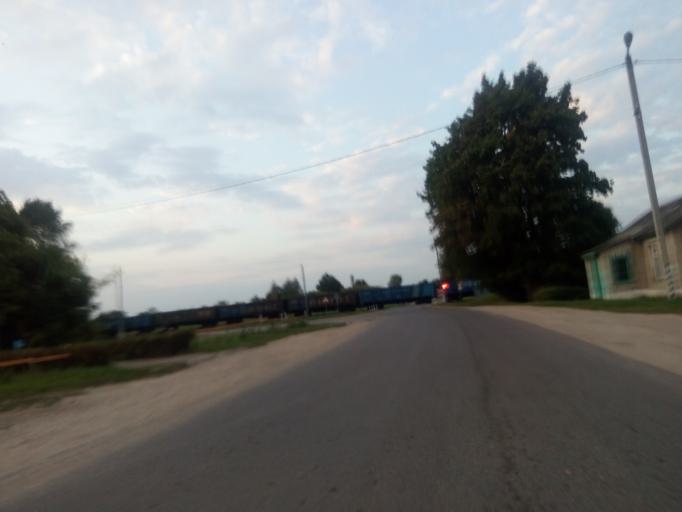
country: BY
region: Vitebsk
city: Dzisna
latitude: 55.6693
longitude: 28.3284
